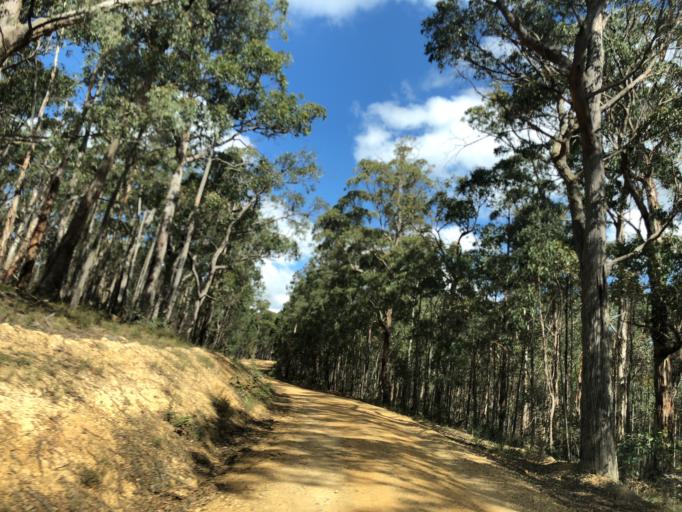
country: AU
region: Victoria
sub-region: Moorabool
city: Bacchus Marsh
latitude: -37.5203
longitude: 144.3213
